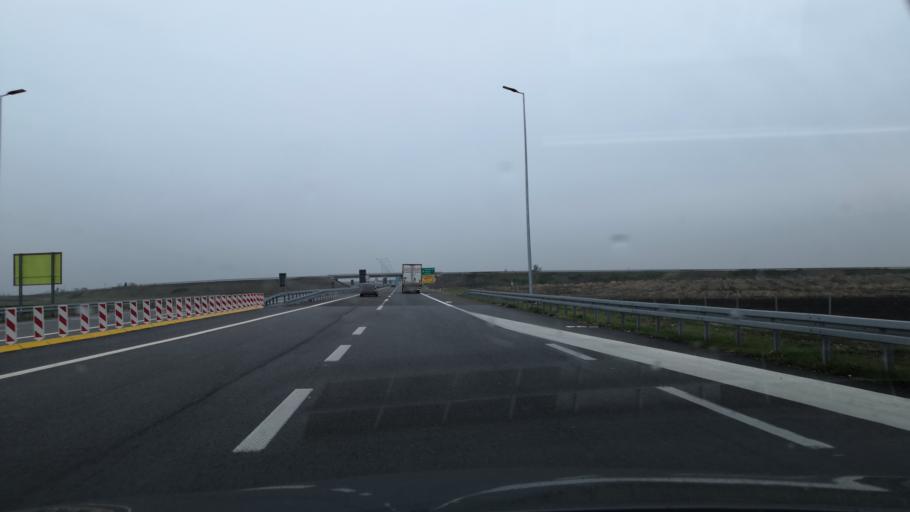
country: RS
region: Autonomna Pokrajina Vojvodina
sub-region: Severnobacki Okrug
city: Subotica
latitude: 46.0225
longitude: 19.7346
